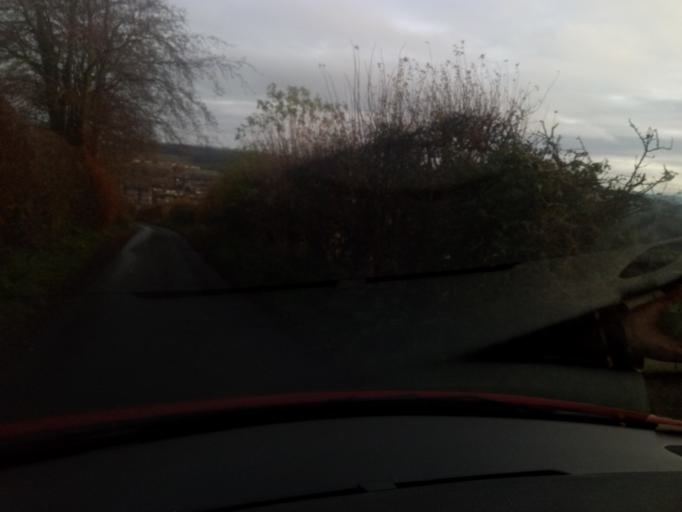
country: GB
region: Scotland
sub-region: The Scottish Borders
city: Jedburgh
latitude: 55.4790
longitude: -2.5656
